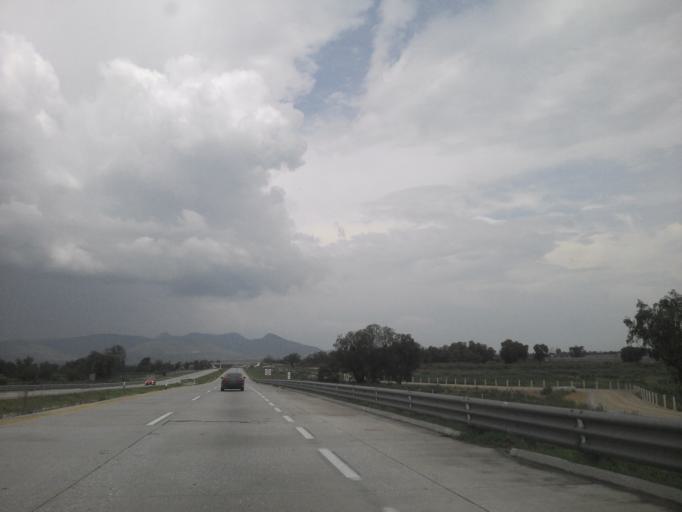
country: MX
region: Hidalgo
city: Doxey
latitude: 20.0823
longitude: -99.2494
